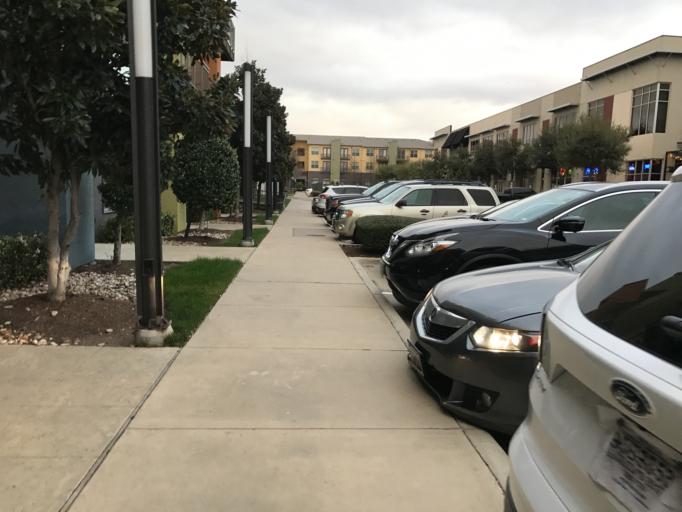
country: US
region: Texas
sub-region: Travis County
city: Austin
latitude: 30.3387
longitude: -97.7190
